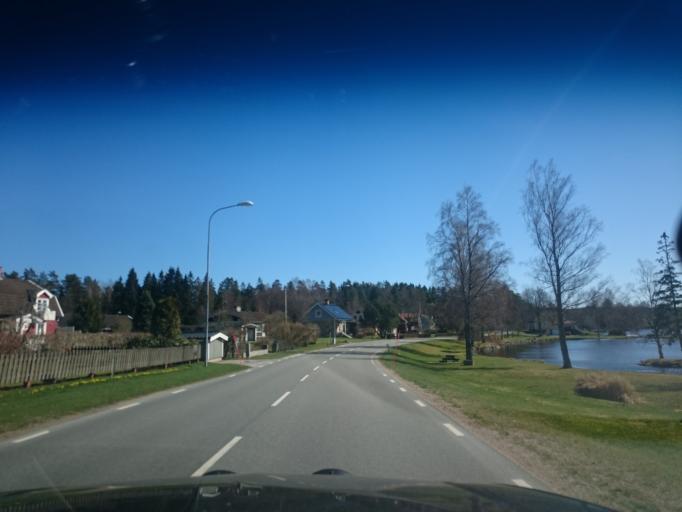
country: SE
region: Kronoberg
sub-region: Vaxjo Kommun
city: Braas
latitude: 57.2030
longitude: 14.9552
